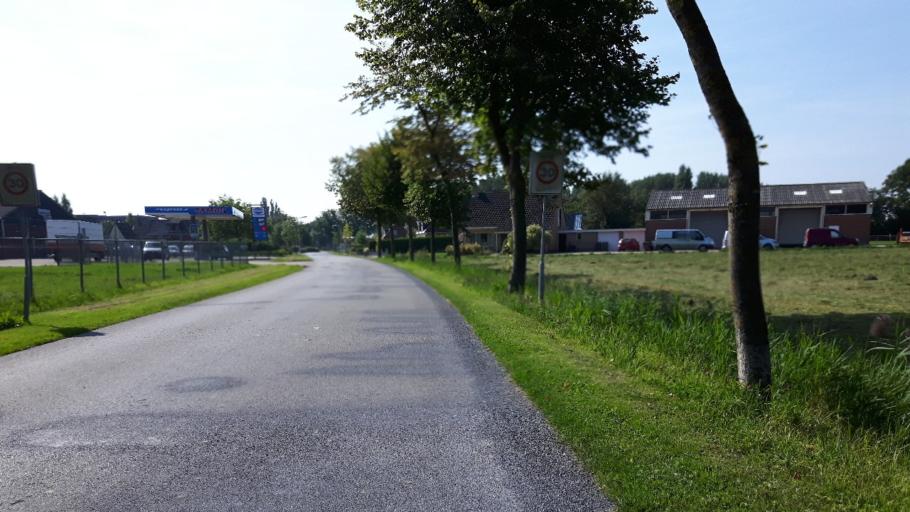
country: NL
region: Friesland
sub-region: Gemeente Ferwerderadiel
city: Marrum
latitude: 53.3278
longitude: 5.8043
